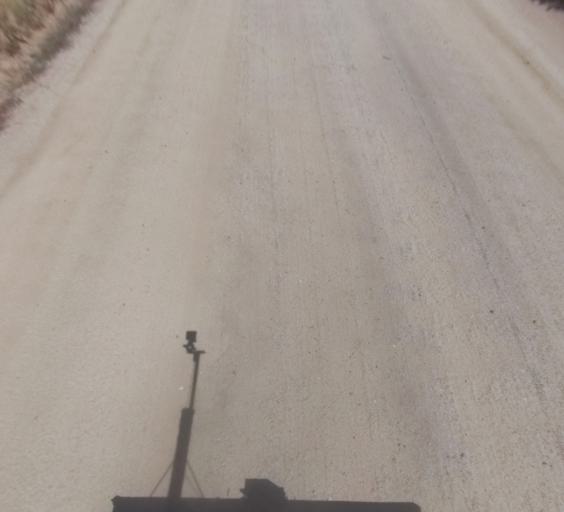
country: US
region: California
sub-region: Madera County
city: Madera Acres
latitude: 37.0820
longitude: -120.0294
